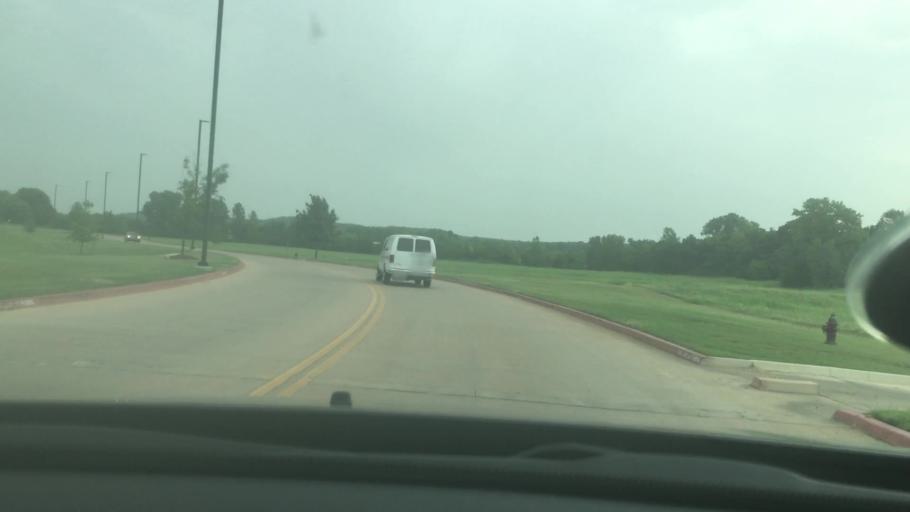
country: US
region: Oklahoma
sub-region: Pontotoc County
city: Ada
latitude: 34.7337
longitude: -96.6470
